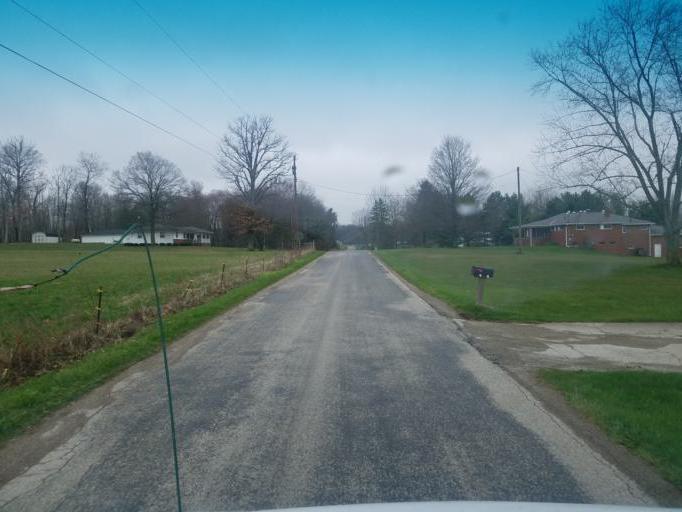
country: US
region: Ohio
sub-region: Richland County
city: Lincoln Heights
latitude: 40.8730
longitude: -82.5078
